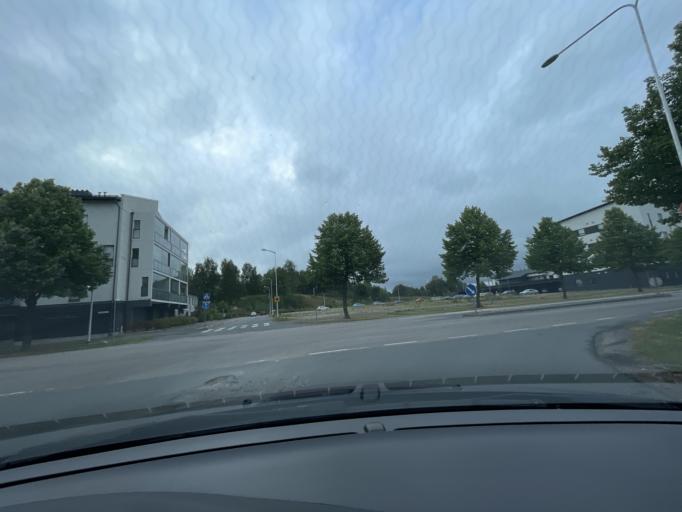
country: FI
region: Haeme
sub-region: Riihimaeki
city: Riihimaeki
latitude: 60.7323
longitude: 24.7726
